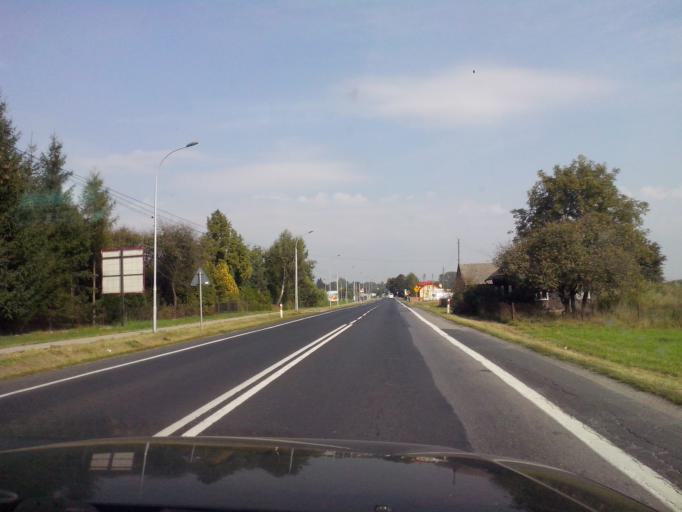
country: PL
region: Subcarpathian Voivodeship
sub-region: Powiat rzeszowski
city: Lutoryz
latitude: 49.9542
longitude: 21.9150
